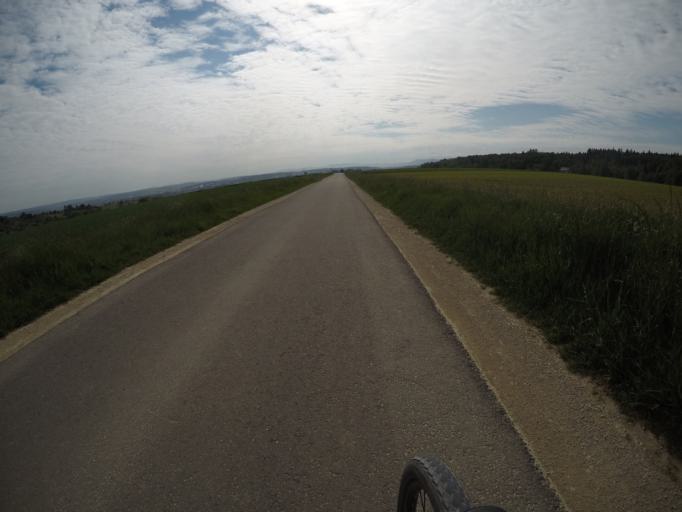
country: DE
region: Baden-Wuerttemberg
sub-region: Regierungsbezirk Stuttgart
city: Unterensingen
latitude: 48.6601
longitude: 9.3280
